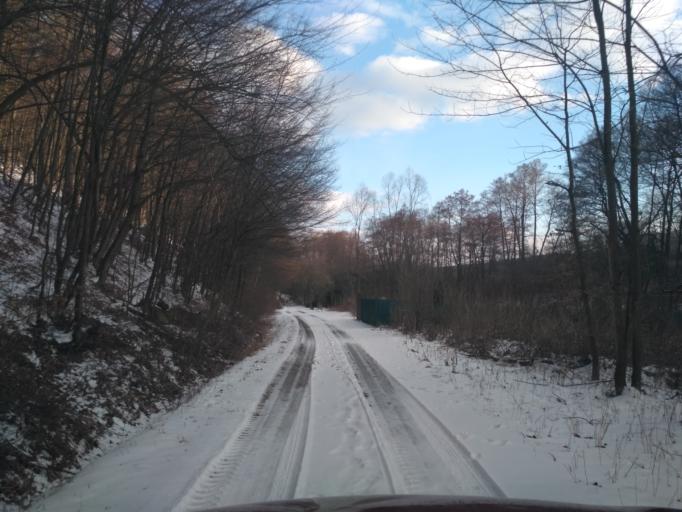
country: SK
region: Kosicky
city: Kosice
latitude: 48.7410
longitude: 21.1540
